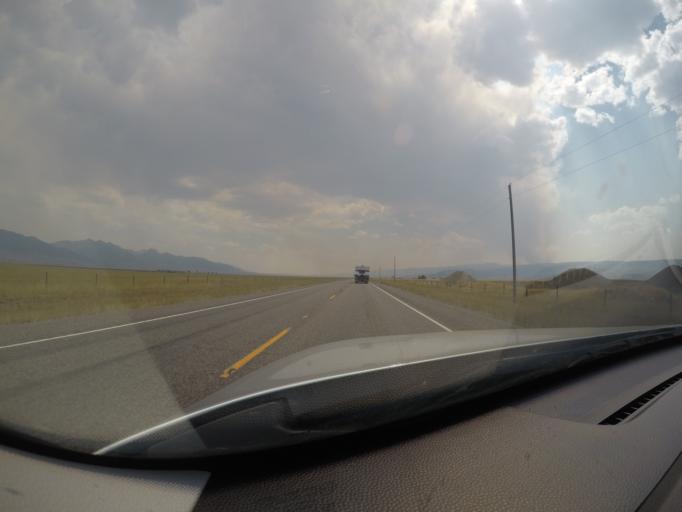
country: US
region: Montana
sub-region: Madison County
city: Virginia City
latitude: 45.1738
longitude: -111.6788
